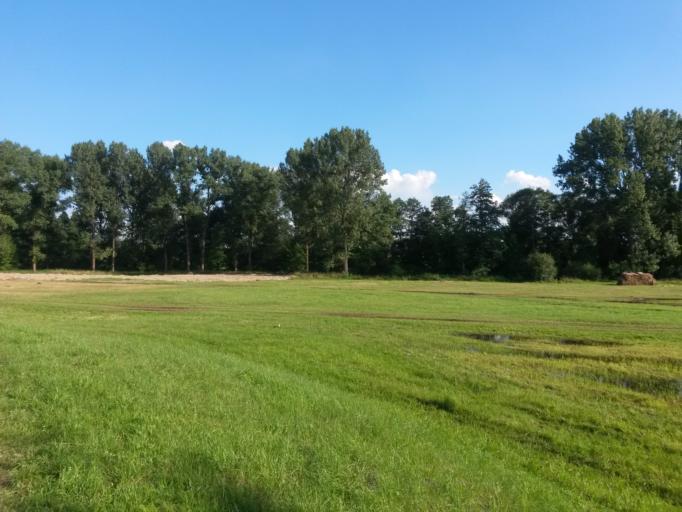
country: PL
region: Silesian Voivodeship
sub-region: Powiat bedzinski
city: Siewierz
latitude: 50.4668
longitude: 19.2411
